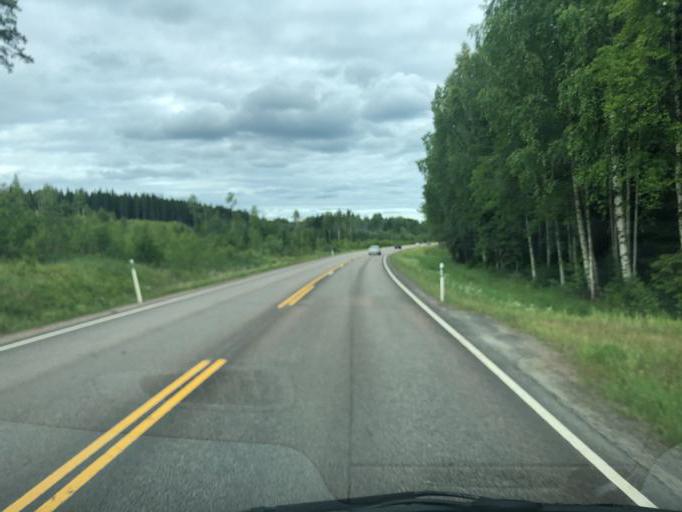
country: FI
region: Kymenlaakso
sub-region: Kouvola
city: Kouvola
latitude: 61.0169
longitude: 26.9544
